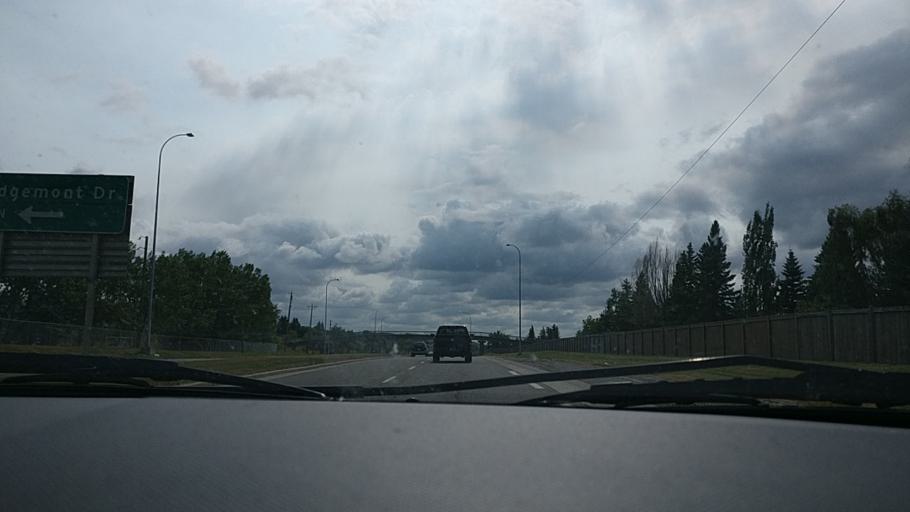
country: CA
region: Alberta
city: Calgary
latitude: 51.1135
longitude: -114.1510
